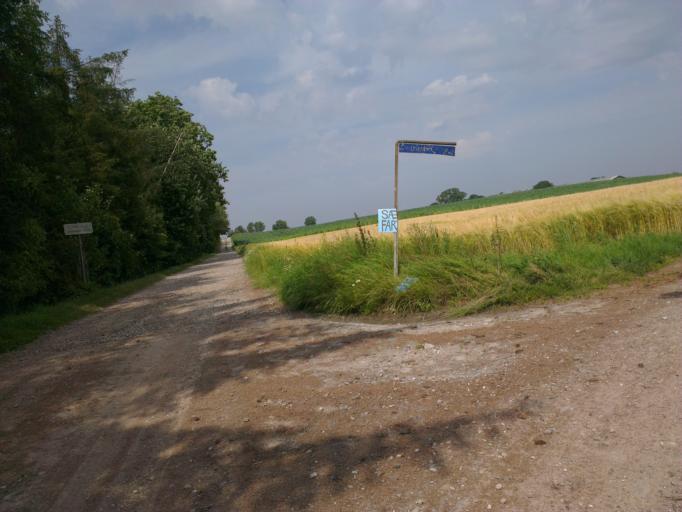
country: DK
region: Capital Region
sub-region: Frederikssund Kommune
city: Skibby
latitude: 55.7769
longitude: 11.9827
